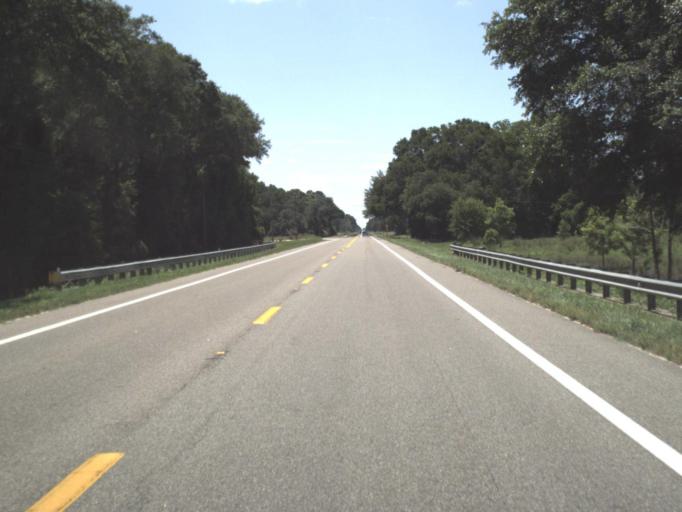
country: US
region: Florida
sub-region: Lafayette County
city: Mayo
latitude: 30.0117
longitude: -83.0350
